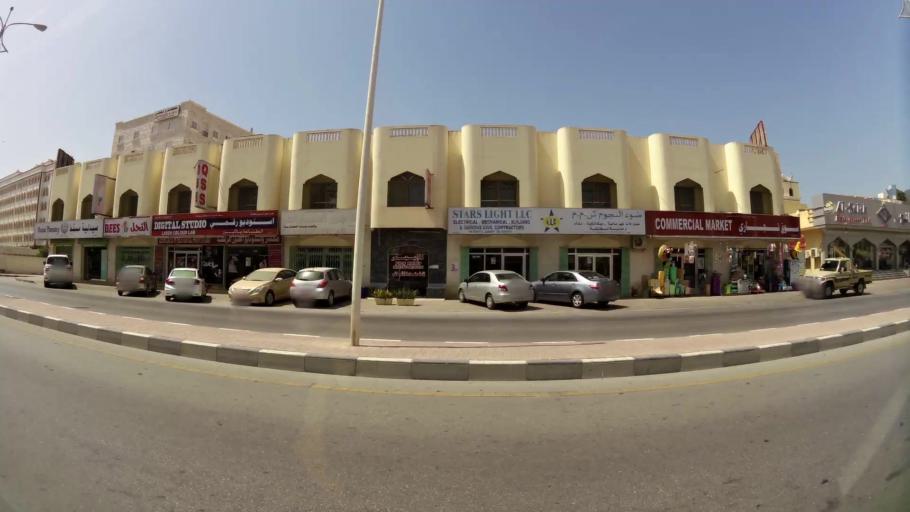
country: OM
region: Zufar
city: Salalah
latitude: 17.0193
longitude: 54.1084
